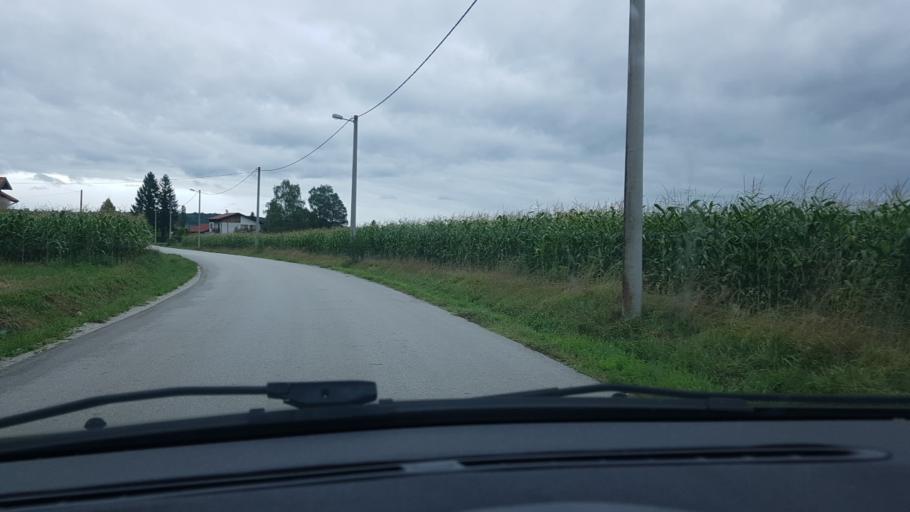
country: HR
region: Karlovacka
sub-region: Grad Karlovac
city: Karlovac
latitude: 45.5540
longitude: 15.5384
